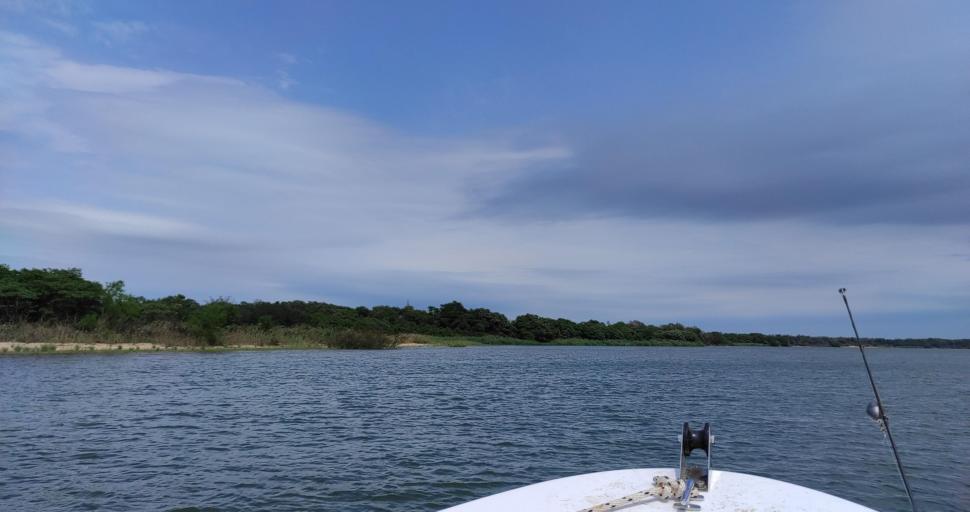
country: PY
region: Neembucu
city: Cerrito
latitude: -27.3460
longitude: -57.6887
